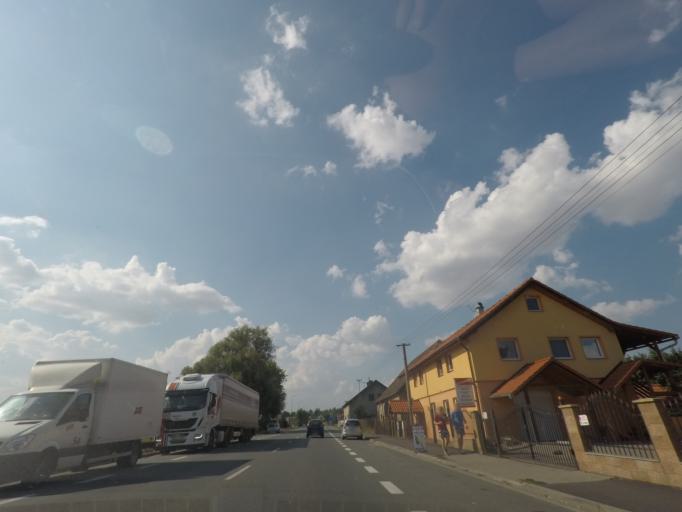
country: CZ
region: Kralovehradecky
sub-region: Okres Nachod
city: Jaromer
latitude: 50.3528
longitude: 15.9082
